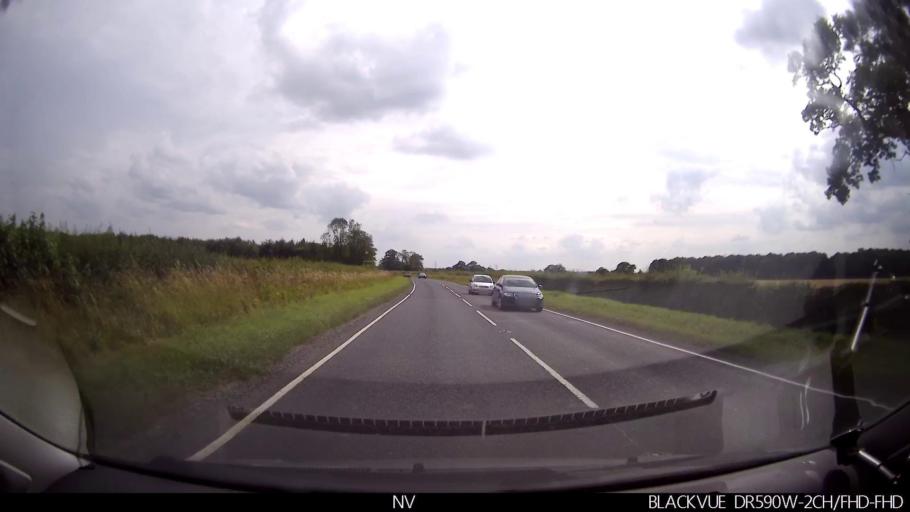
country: GB
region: England
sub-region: North Yorkshire
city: Malton
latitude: 54.1629
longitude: -0.7677
